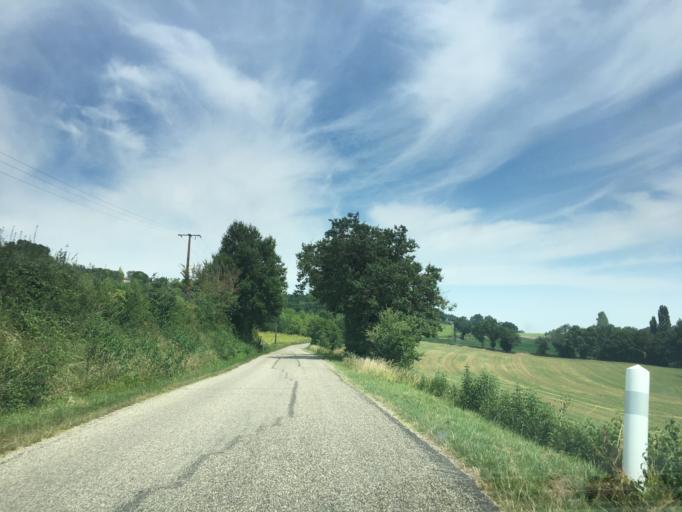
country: FR
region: Midi-Pyrenees
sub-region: Departement du Gers
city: Jegun
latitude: 43.8113
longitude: 0.5157
